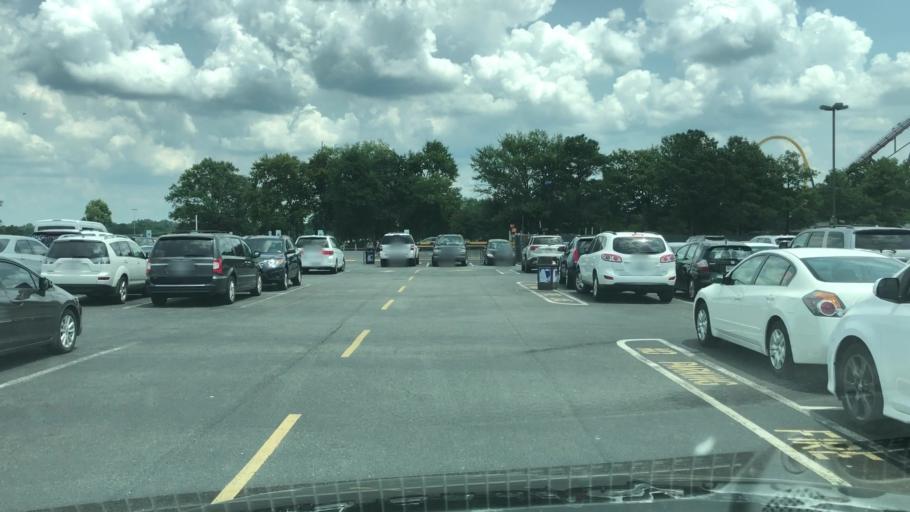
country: US
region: Virginia
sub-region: Hanover County
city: Ashland
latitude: 37.8423
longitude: -77.4473
